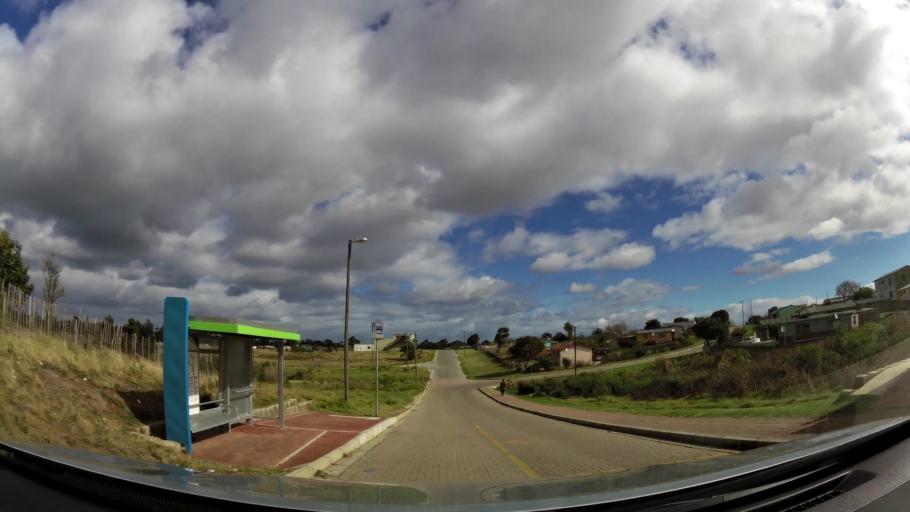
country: ZA
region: Western Cape
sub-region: Eden District Municipality
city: George
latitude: -34.0237
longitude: 22.4690
